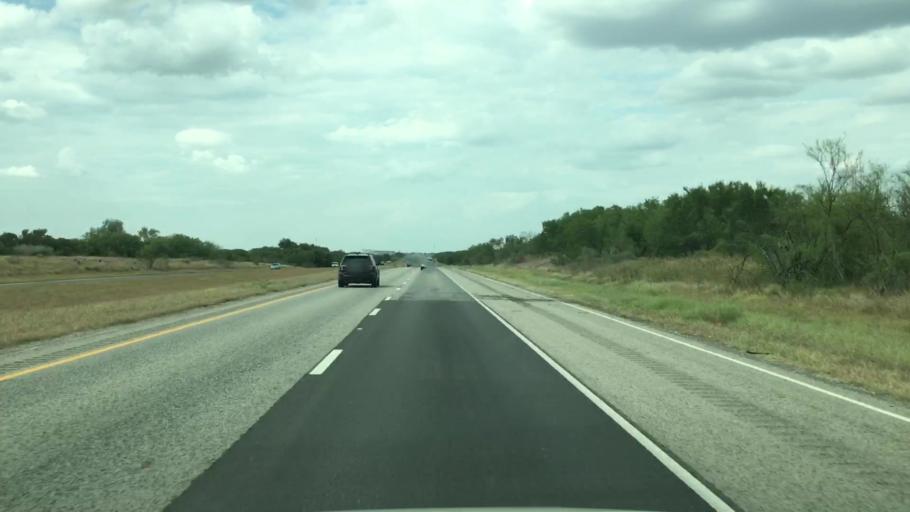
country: US
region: Texas
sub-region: Atascosa County
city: Pleasanton
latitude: 29.0729
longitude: -98.4329
